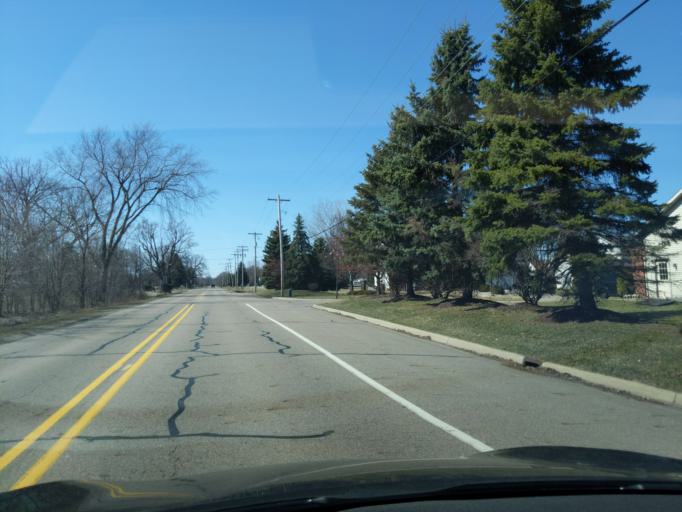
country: US
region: Michigan
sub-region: Eaton County
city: Waverly
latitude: 42.7266
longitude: -84.6854
